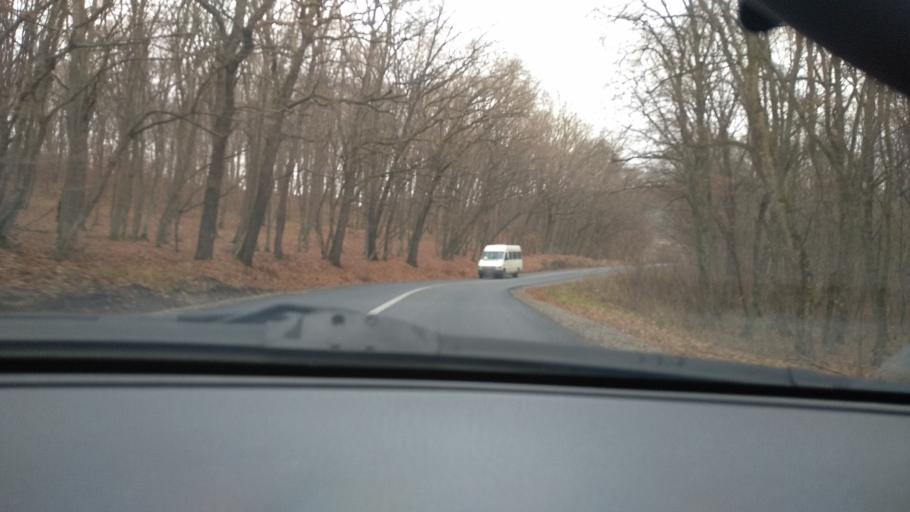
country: RO
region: Mures
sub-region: Comuna Pasareni
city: Pasareni
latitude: 46.5330
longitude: 24.6981
